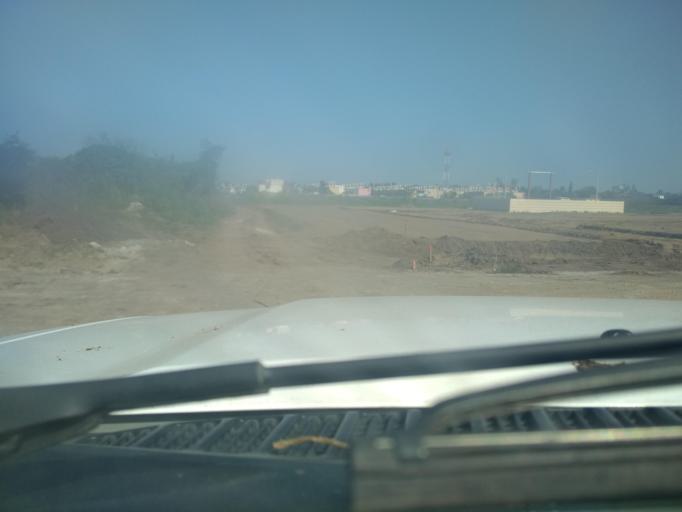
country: MX
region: Veracruz
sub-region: Veracruz
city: Las Amapolas
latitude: 19.1514
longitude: -96.2071
